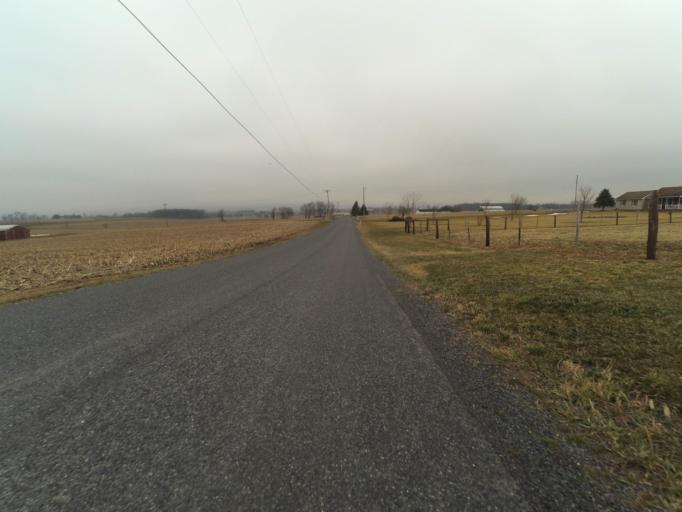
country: US
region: Pennsylvania
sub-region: Centre County
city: Centre Hall
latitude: 40.7954
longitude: -77.7025
